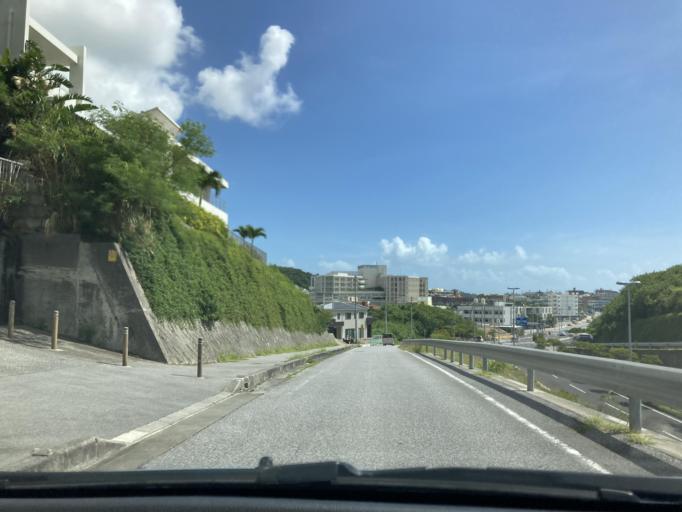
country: JP
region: Okinawa
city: Naha-shi
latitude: 26.2044
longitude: 127.7189
